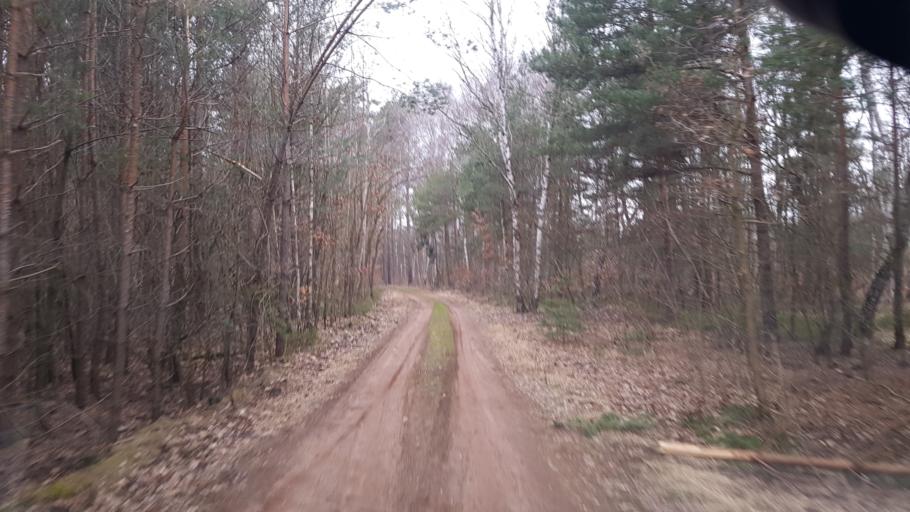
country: DE
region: Brandenburg
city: Trobitz
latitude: 51.6150
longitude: 13.4512
